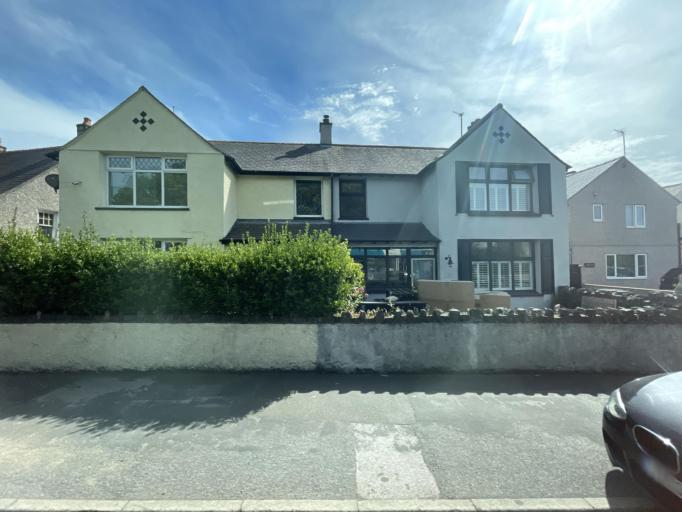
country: GB
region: Wales
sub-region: Anglesey
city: Holyhead
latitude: 53.3032
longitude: -4.6207
